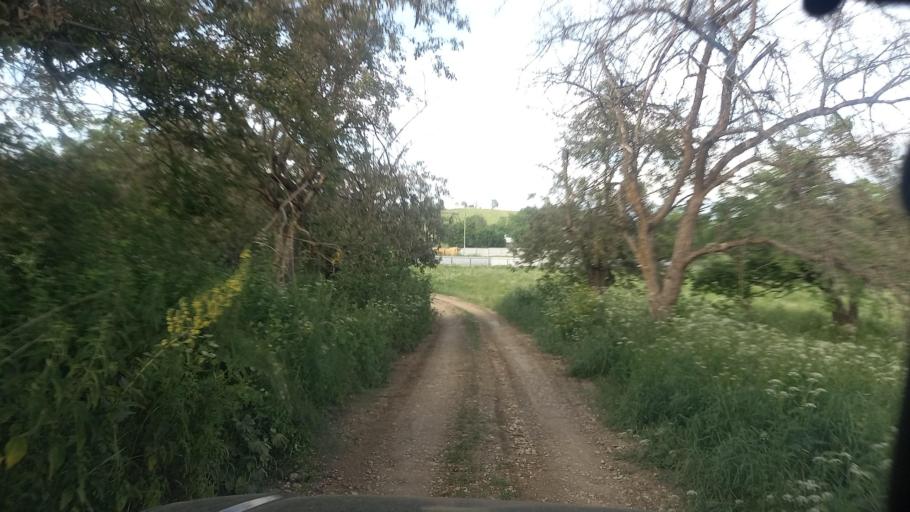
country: RU
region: Krasnodarskiy
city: Peredovaya
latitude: 44.0818
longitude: 41.3668
